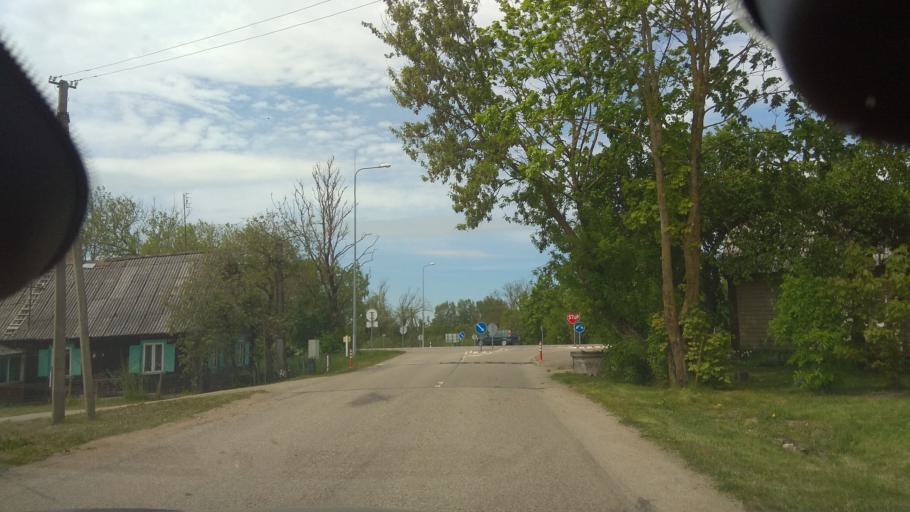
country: LT
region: Kauno apskritis
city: Jonava
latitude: 55.1639
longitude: 24.5125
